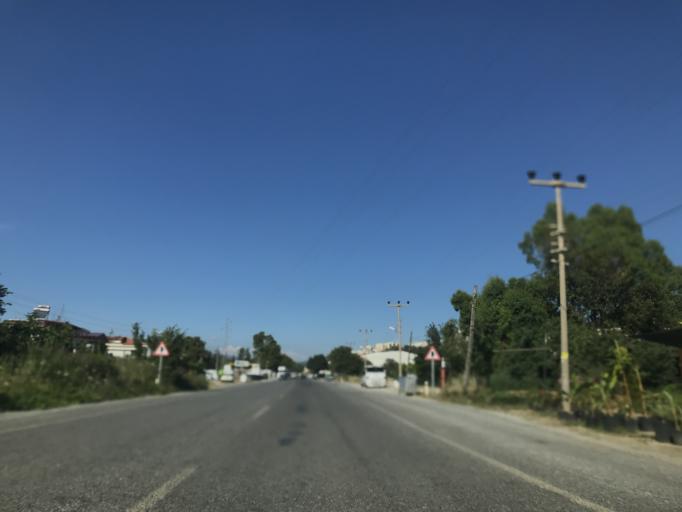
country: TR
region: Aydin
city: Davutlar
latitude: 37.7191
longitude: 27.2460
